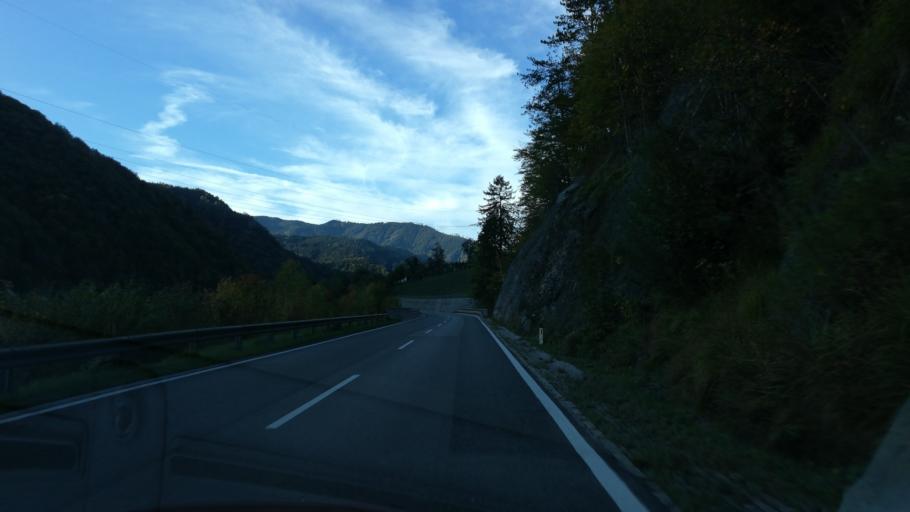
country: AT
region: Styria
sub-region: Politischer Bezirk Liezen
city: Altenmarkt bei Sankt Gallen
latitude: 47.7808
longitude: 14.6529
